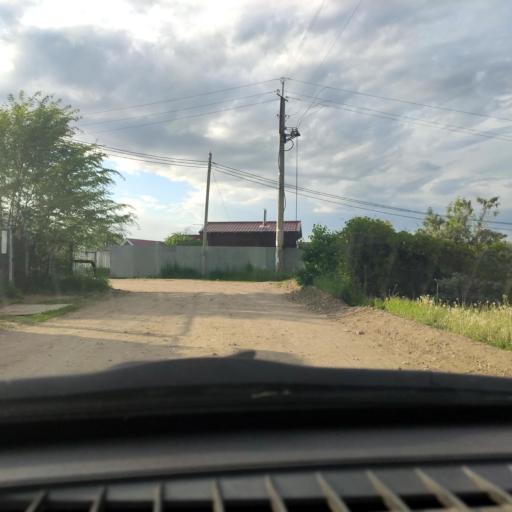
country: RU
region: Samara
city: Zhigulevsk
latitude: 53.4486
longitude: 49.5461
